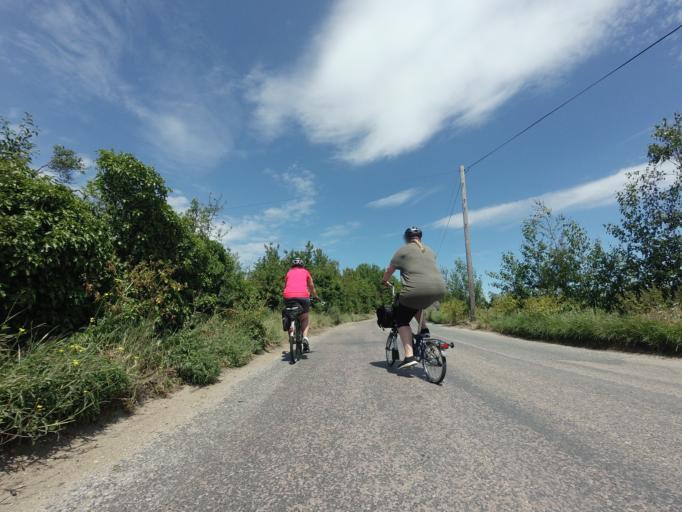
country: GB
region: England
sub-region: Kent
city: Cliffe
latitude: 51.4519
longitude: 0.4902
